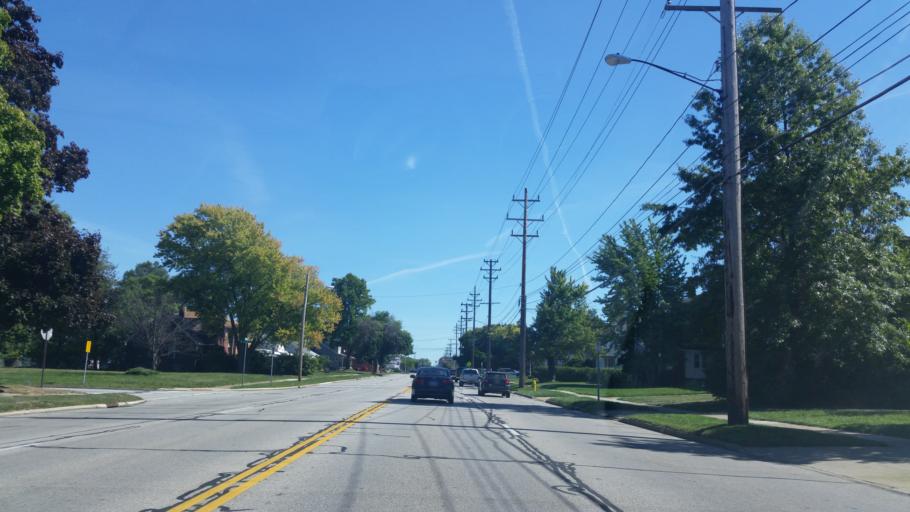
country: US
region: Ohio
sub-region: Cuyahoga County
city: Parma
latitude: 41.4049
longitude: -81.7145
